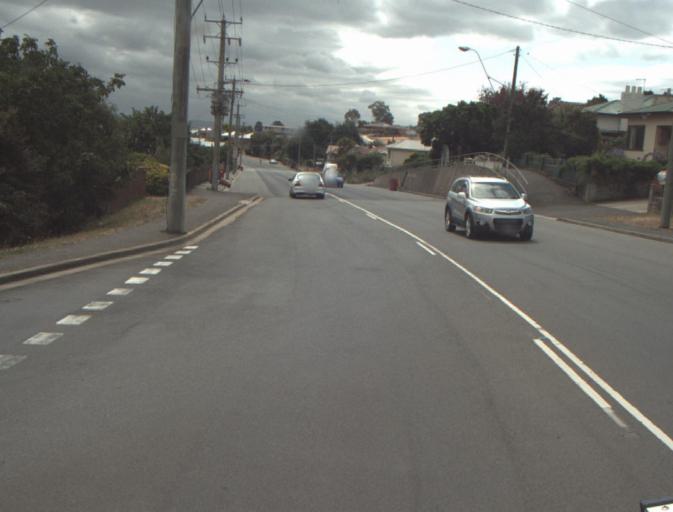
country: AU
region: Tasmania
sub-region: Launceston
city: Newstead
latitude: -41.4550
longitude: 147.1989
